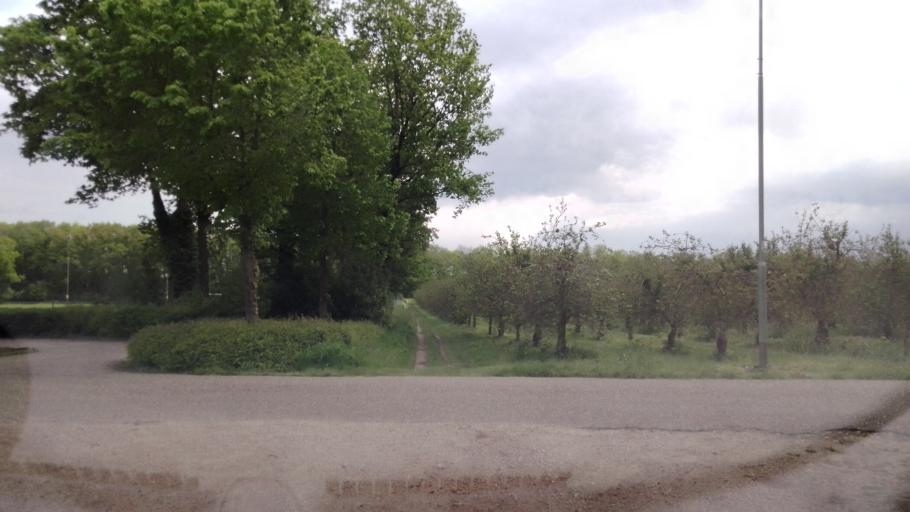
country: NL
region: Limburg
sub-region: Gemeente Beesel
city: Beesel
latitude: 51.2648
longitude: 6.0315
